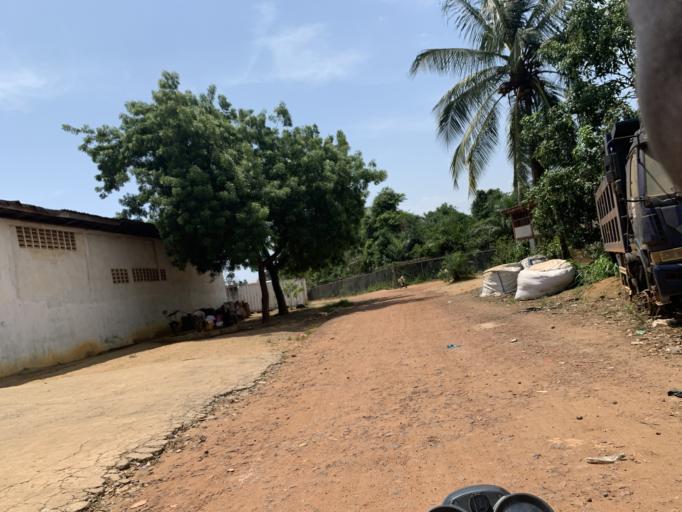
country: SL
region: Western Area
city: Waterloo
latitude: 8.3360
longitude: -13.0345
